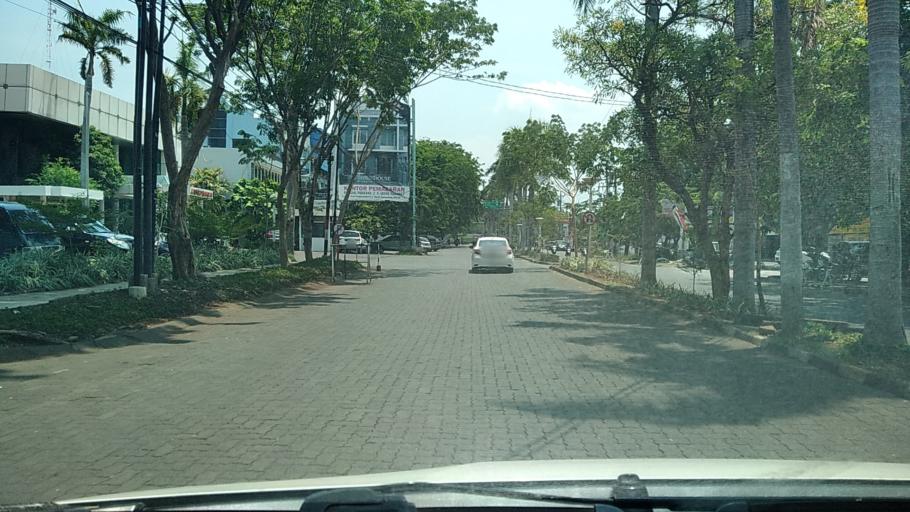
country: ID
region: Central Java
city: Semarang
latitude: -6.9685
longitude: 110.3906
